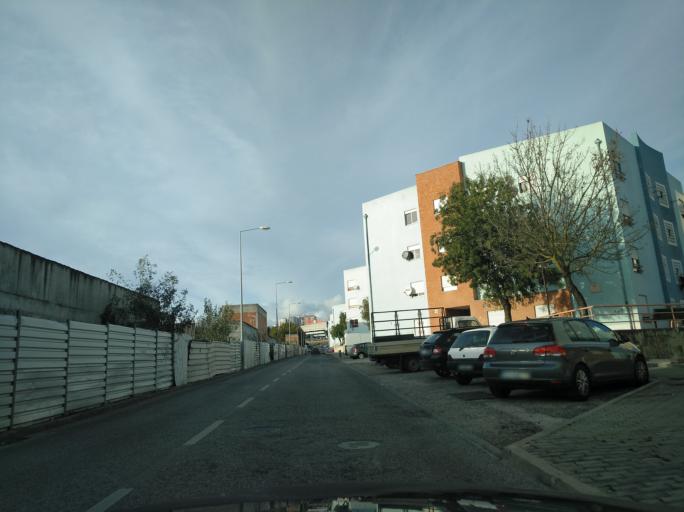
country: PT
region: Lisbon
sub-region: Oeiras
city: Alges
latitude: 38.7234
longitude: -9.2218
